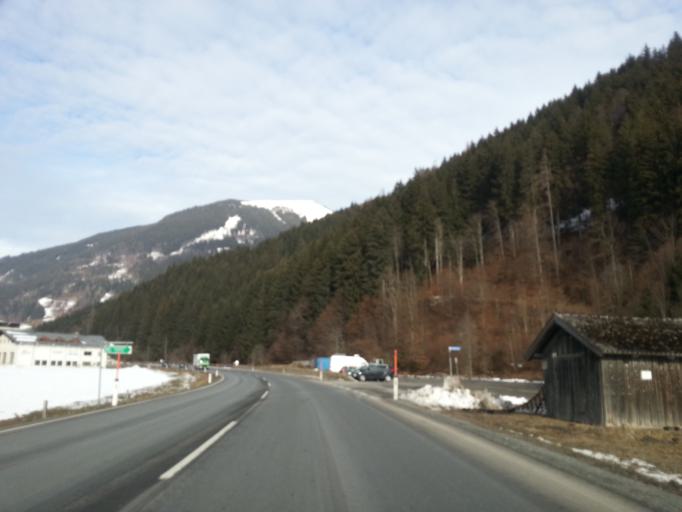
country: AT
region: Salzburg
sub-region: Politischer Bezirk Zell am See
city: Maishofen
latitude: 47.3620
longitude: 12.7949
